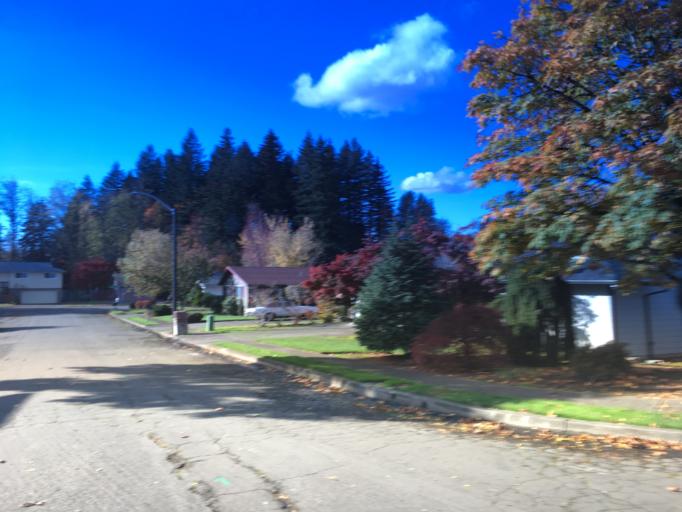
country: US
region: Oregon
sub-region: Multnomah County
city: Gresham
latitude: 45.5021
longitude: -122.3959
